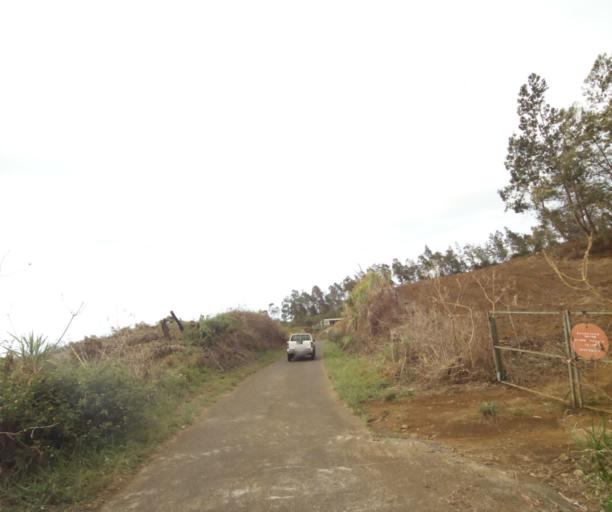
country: RE
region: Reunion
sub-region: Reunion
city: Saint-Paul
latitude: -21.0145
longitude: 55.3482
